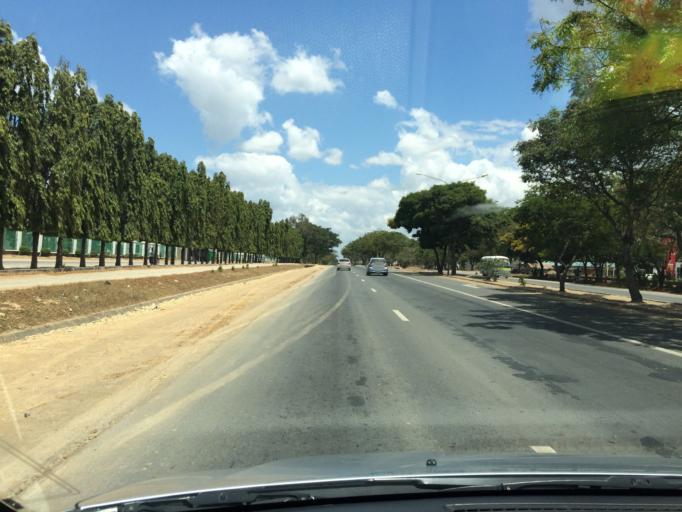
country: TZ
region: Dar es Salaam
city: Dar es Salaam
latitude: -6.8410
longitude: 39.2521
